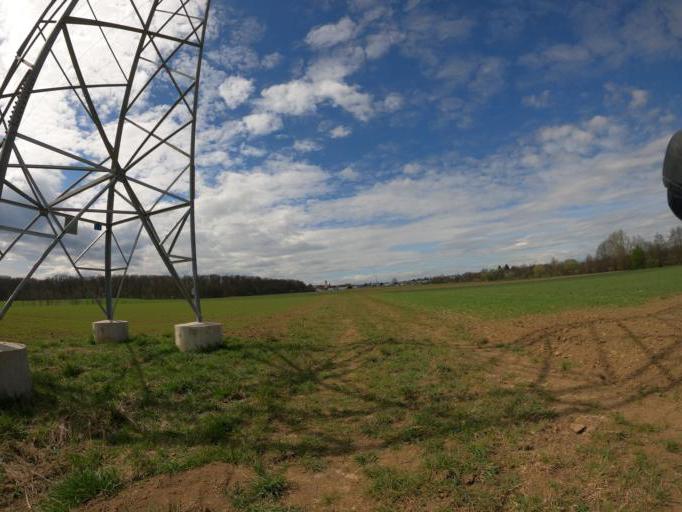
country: DE
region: Baden-Wuerttemberg
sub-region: Tuebingen Region
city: Kusterdingen
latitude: 48.4894
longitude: 9.1237
